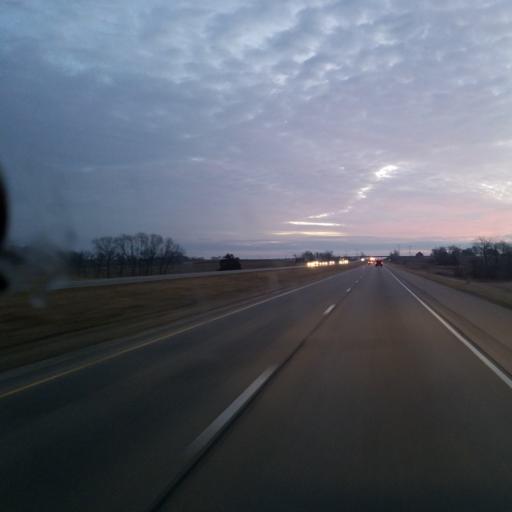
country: US
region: Illinois
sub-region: Tazewell County
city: Morton
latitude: 40.6215
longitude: -89.4134
